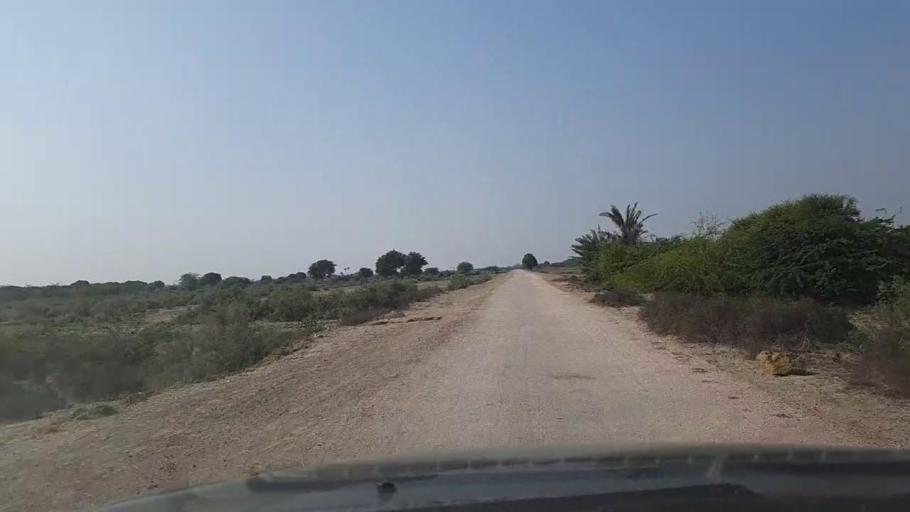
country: PK
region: Sindh
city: Mirpur Sakro
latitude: 24.4061
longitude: 67.6872
